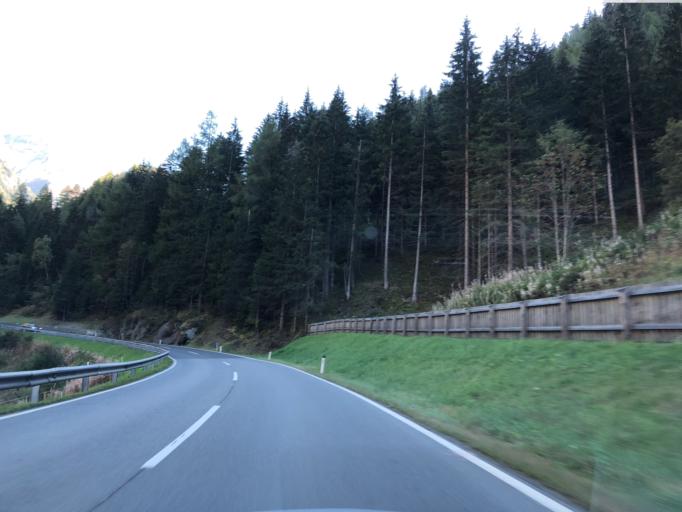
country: AT
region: Tyrol
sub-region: Politischer Bezirk Imst
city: Soelden
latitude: 47.0107
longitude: 11.0014
